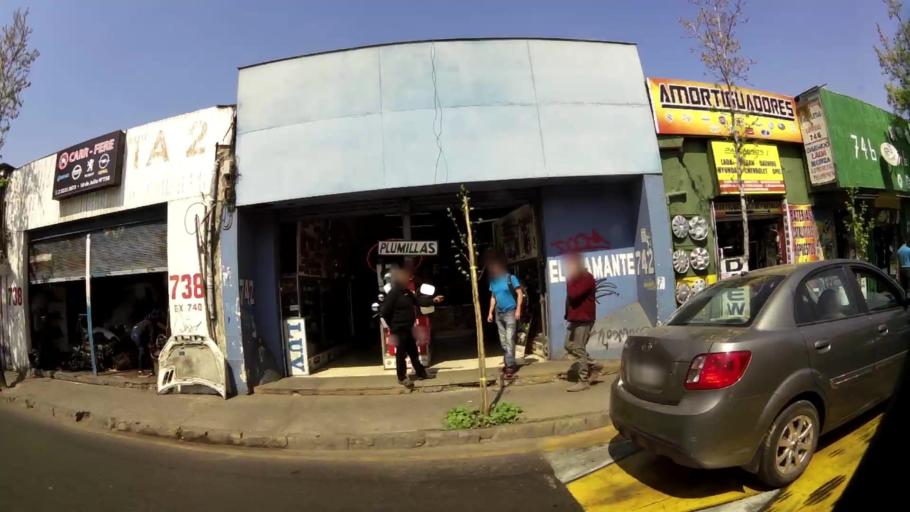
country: CL
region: Santiago Metropolitan
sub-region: Provincia de Santiago
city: Santiago
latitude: -33.4534
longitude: -70.6451
